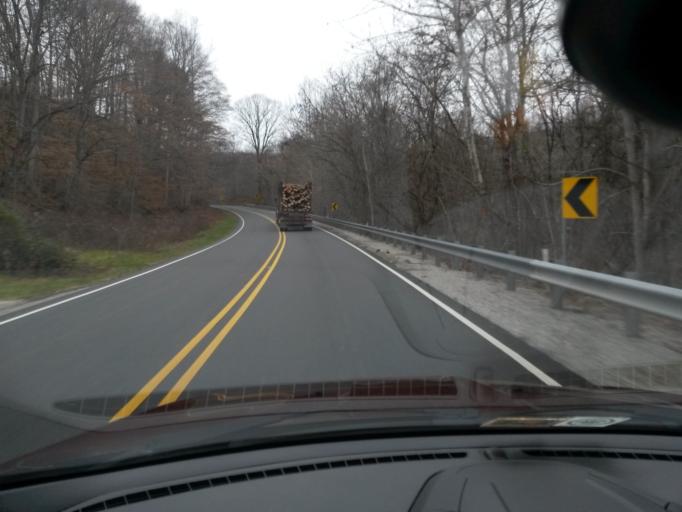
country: US
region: Virginia
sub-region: City of Buena Vista
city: Buena Vista
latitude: 37.6857
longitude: -79.2291
